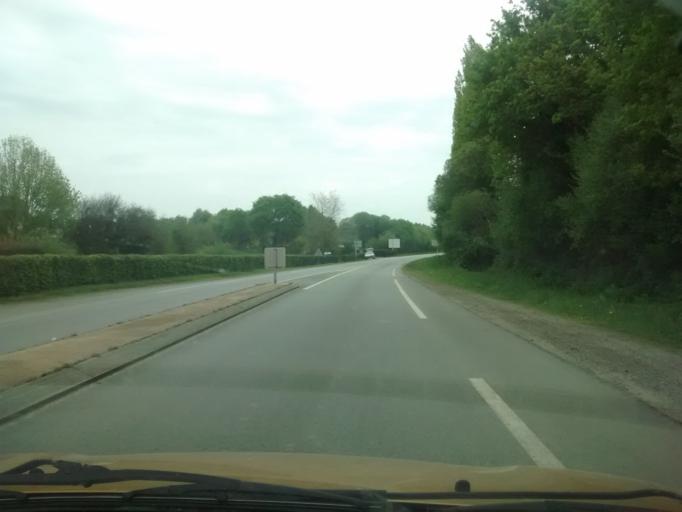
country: FR
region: Brittany
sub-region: Departement du Morbihan
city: Berric
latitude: 47.6153
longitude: -2.5396
